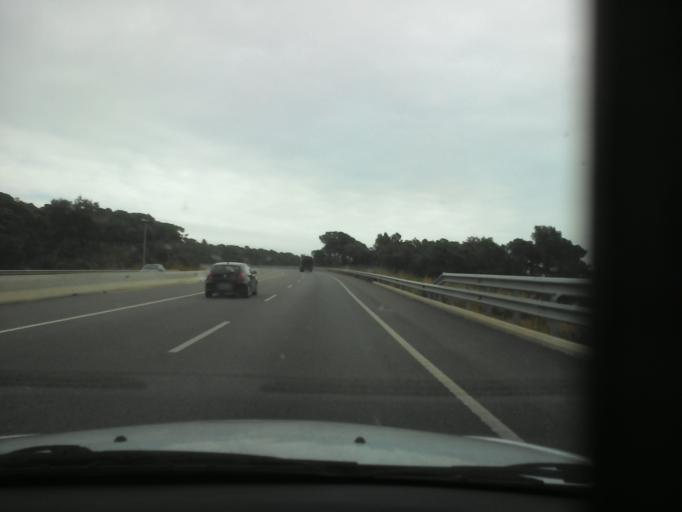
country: ES
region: Catalonia
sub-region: Provincia de Girona
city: Calonge
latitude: 41.8399
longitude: 3.0742
